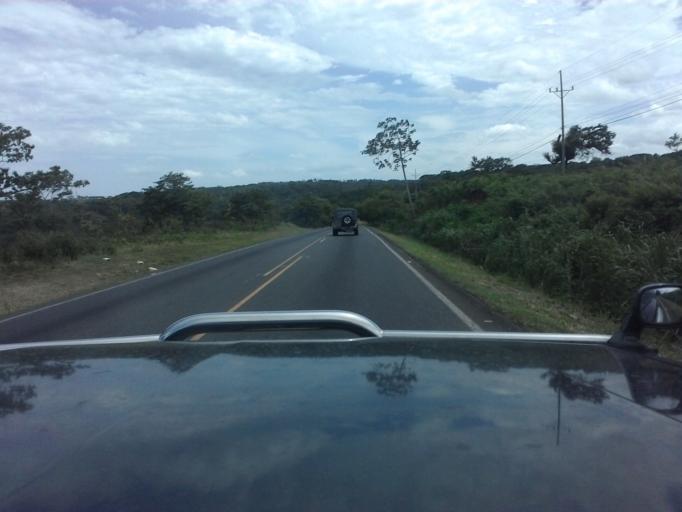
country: CR
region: Puntarenas
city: Miramar
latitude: 10.0975
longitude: -84.8024
